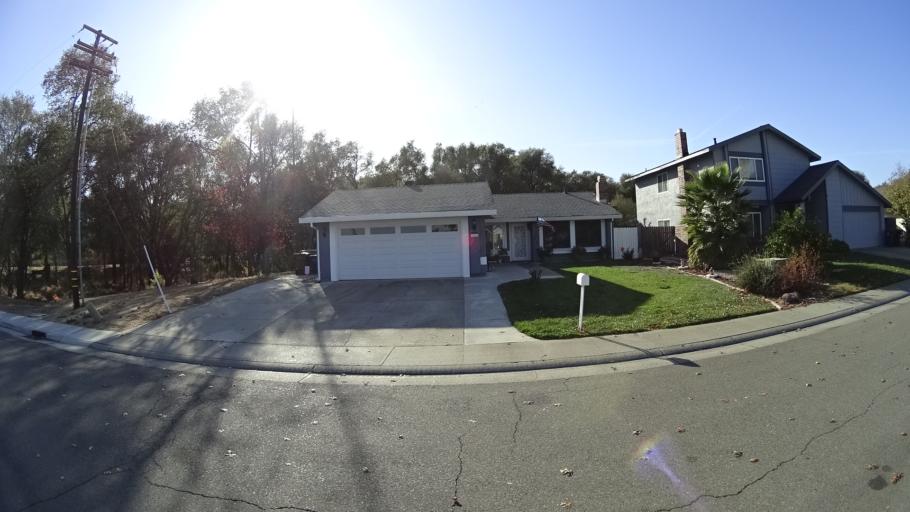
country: US
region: California
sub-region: Sacramento County
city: Antelope
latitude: 38.6973
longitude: -121.3128
